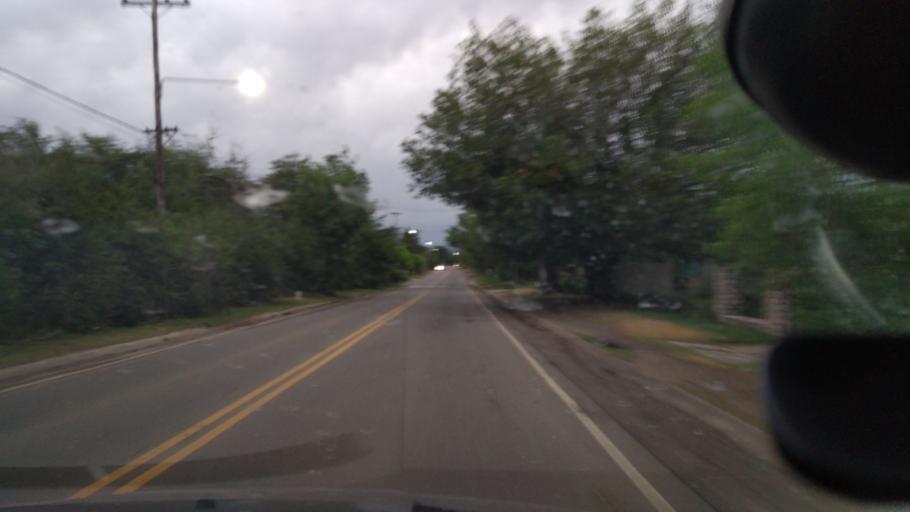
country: AR
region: Cordoba
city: Villa Las Rosas
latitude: -31.9157
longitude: -65.0368
